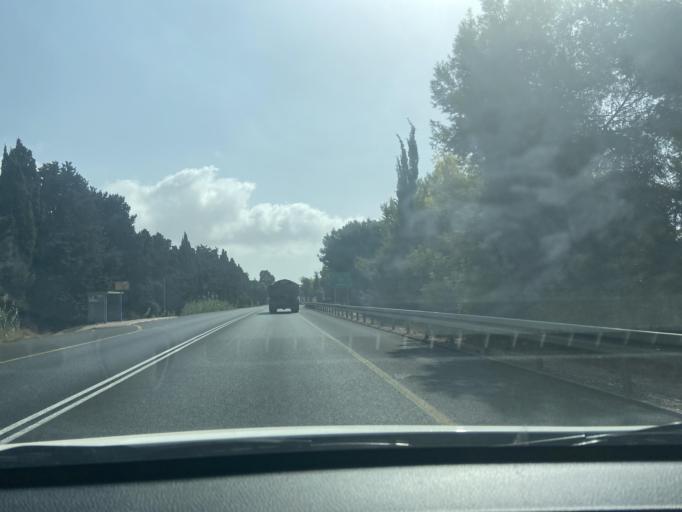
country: IL
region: Northern District
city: Nahariya
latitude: 33.0382
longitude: 35.1057
